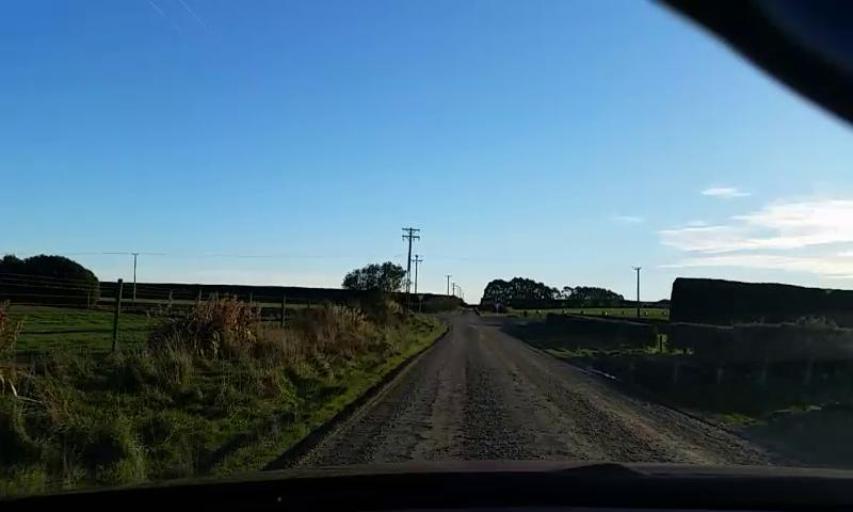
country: NZ
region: Southland
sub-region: Invercargill City
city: Invercargill
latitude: -46.2851
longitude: 168.4805
